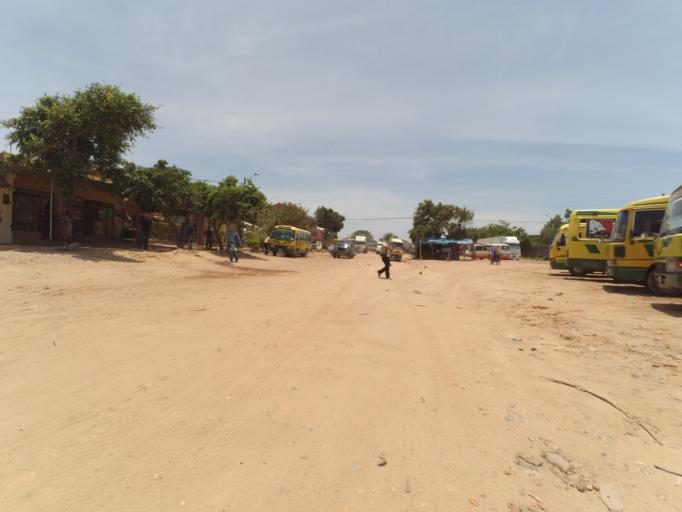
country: BO
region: Santa Cruz
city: Santa Cruz de la Sierra
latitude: -17.8318
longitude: -63.2419
